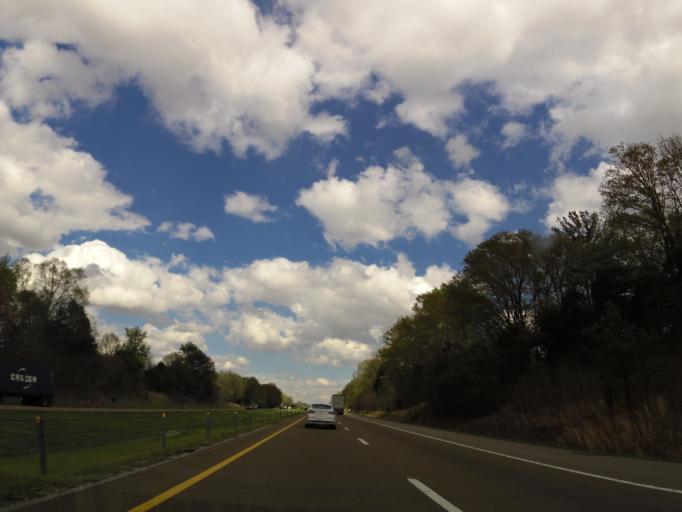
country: US
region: Tennessee
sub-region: Crockett County
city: Bells
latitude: 35.6127
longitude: -89.0137
